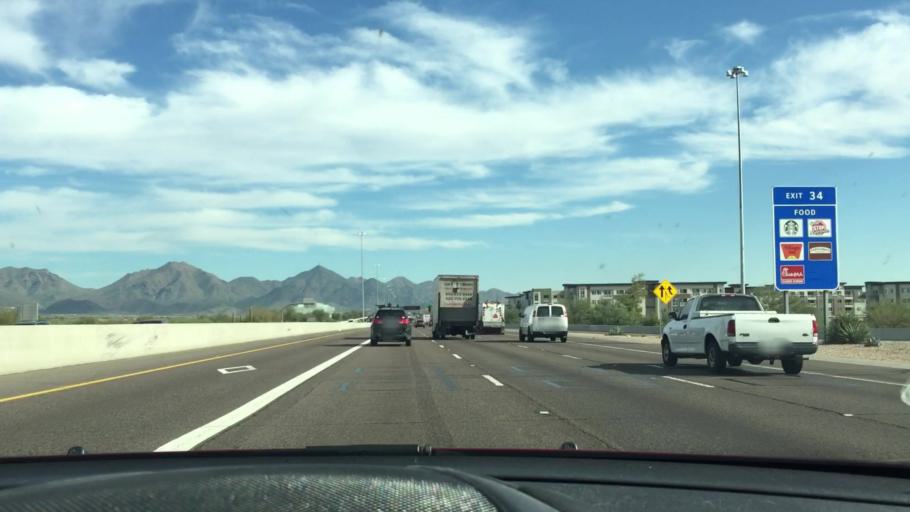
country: US
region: Arizona
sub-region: Maricopa County
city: Paradise Valley
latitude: 33.6618
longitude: -111.9385
